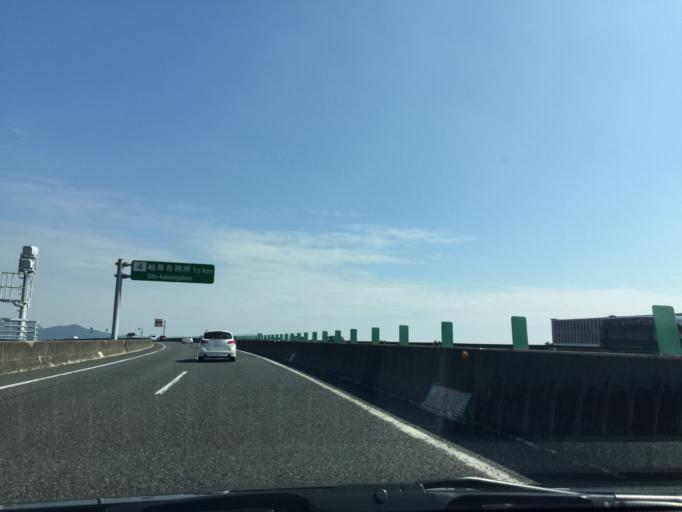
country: JP
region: Aichi
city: Kuroda
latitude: 35.3723
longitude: 136.8135
